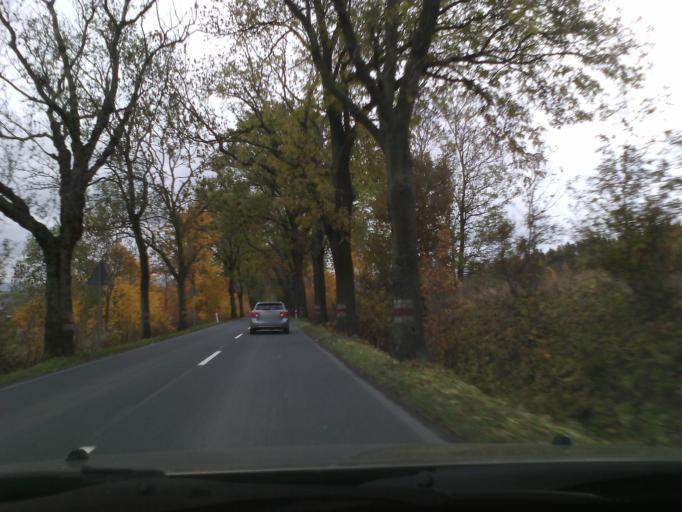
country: PL
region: Lower Silesian Voivodeship
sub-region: Powiat kamiennogorski
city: Kamienna Gora
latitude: 50.7778
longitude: 15.9515
